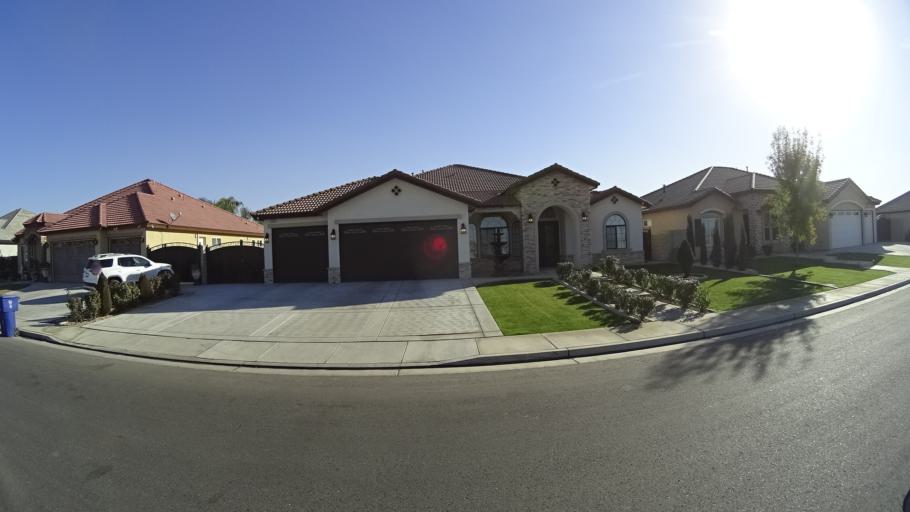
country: US
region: California
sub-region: Kern County
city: Greenfield
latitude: 35.2707
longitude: -119.0451
